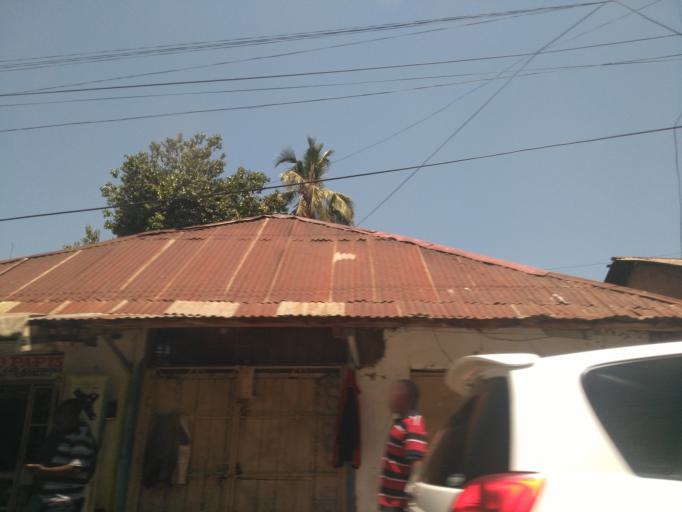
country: TZ
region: Mwanza
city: Mwanza
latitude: -2.5228
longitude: 32.9013
